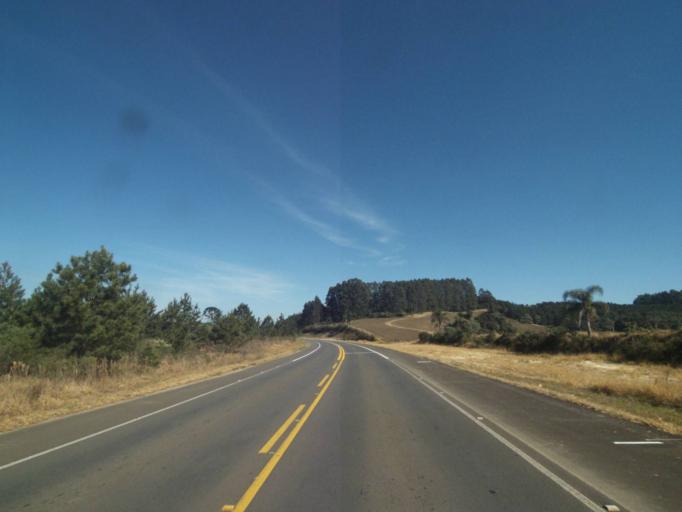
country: BR
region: Parana
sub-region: Tibagi
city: Tibagi
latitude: -24.8089
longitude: -50.4799
